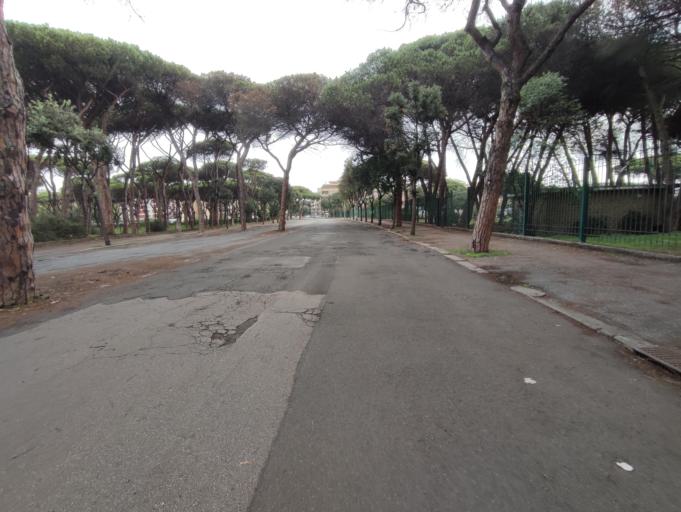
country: IT
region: Latium
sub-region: Citta metropolitana di Roma Capitale
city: Lido di Ostia
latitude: 41.7317
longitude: 12.2991
